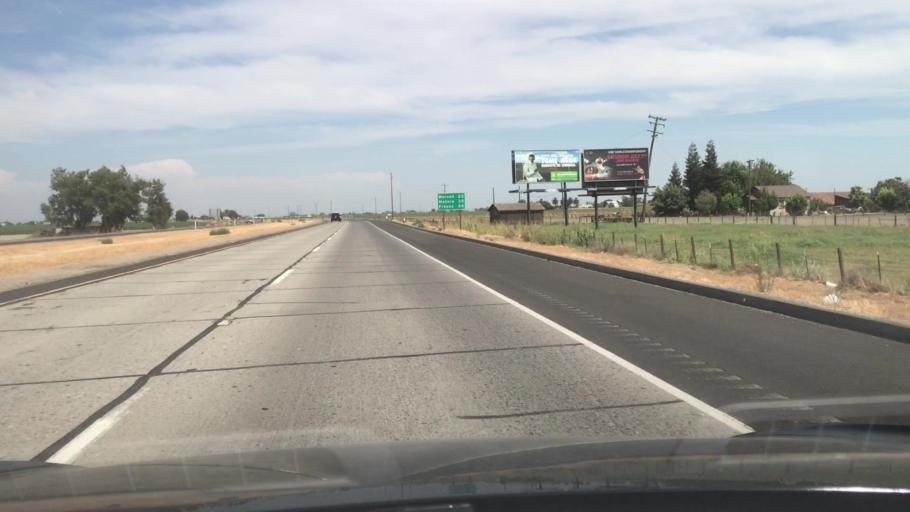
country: US
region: California
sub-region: Merced County
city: Dos Palos
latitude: 37.0486
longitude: -120.6268
